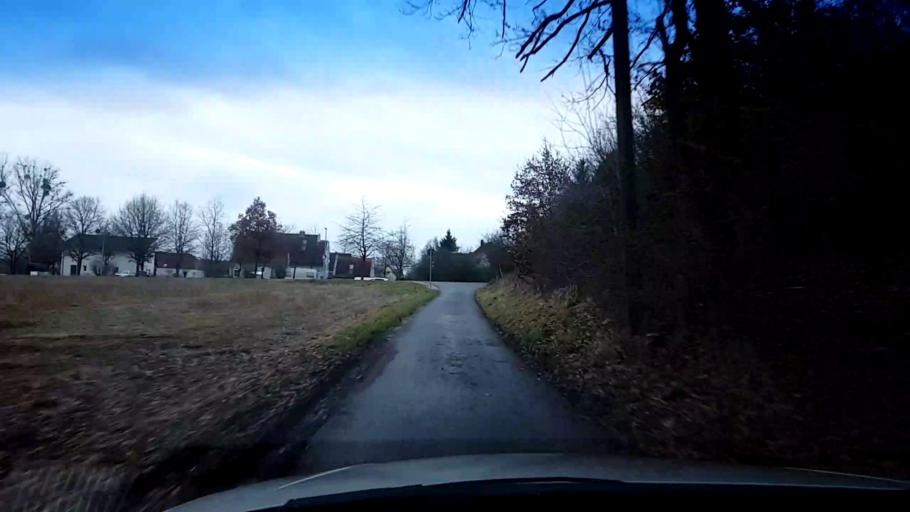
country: DE
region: Bavaria
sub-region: Upper Franconia
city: Hallstadt
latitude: 49.9353
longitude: 10.8649
